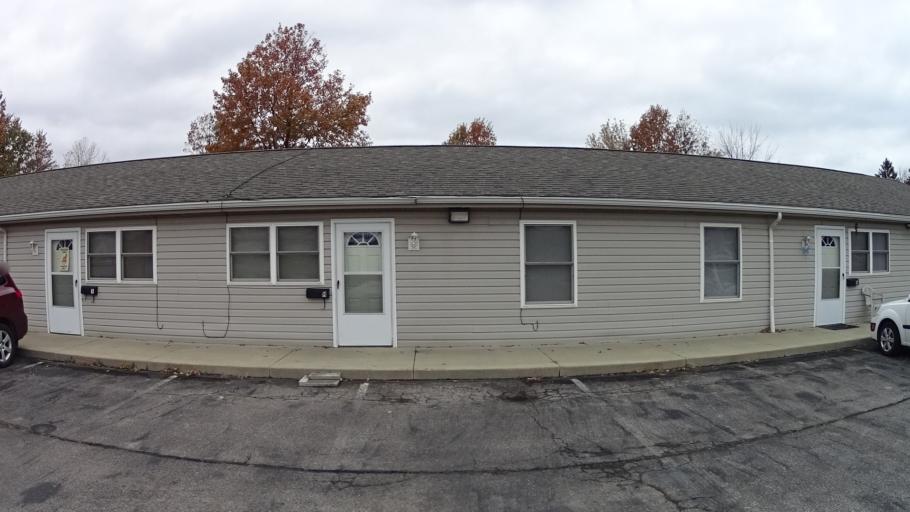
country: US
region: Ohio
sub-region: Lorain County
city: Amherst
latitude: 41.4410
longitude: -82.2266
